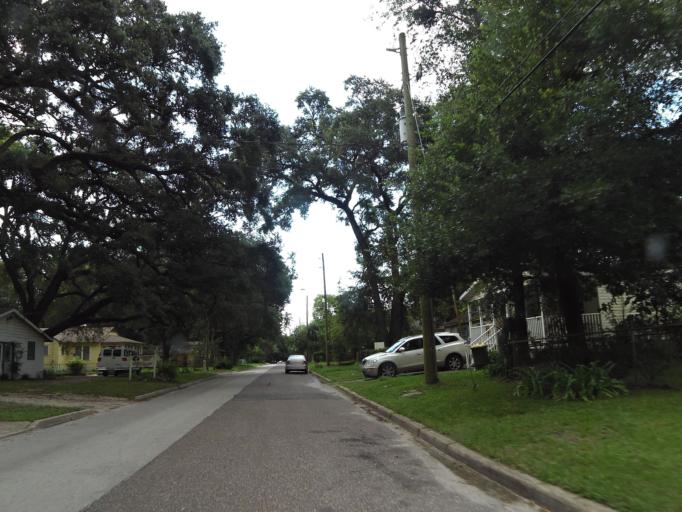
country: US
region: Florida
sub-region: Duval County
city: Jacksonville
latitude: 30.3536
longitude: -81.6353
